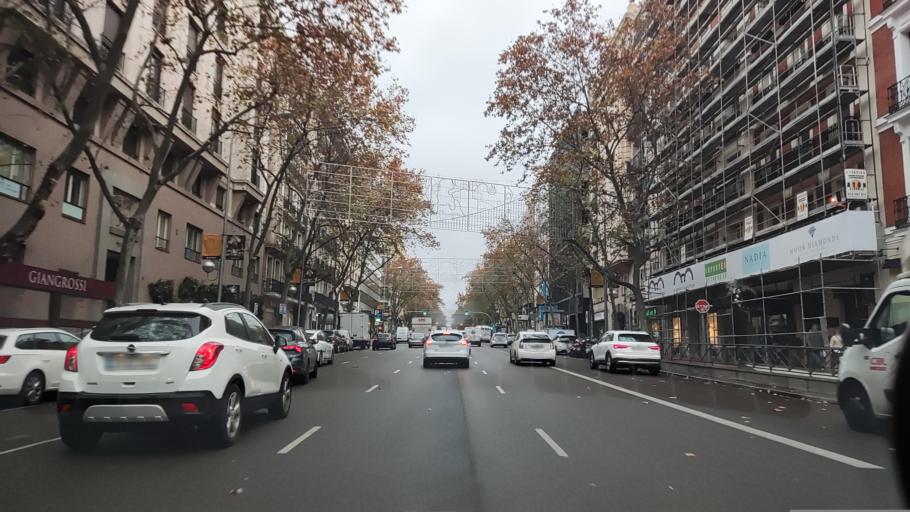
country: ES
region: Madrid
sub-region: Provincia de Madrid
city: Salamanca
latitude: 40.4264
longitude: -3.6840
